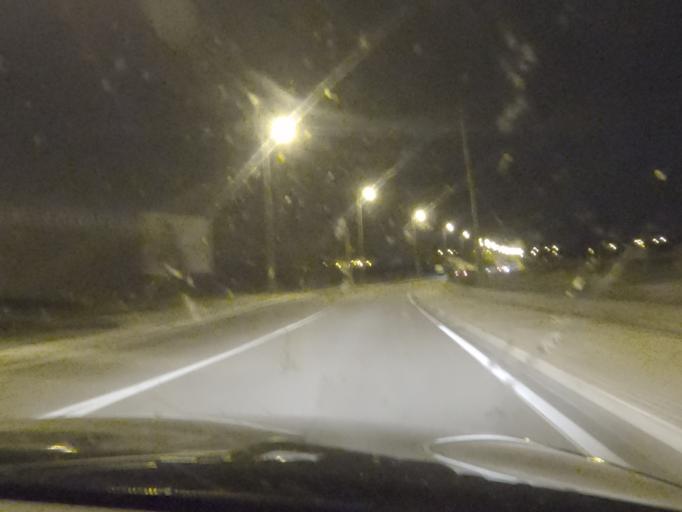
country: PT
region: Evora
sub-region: Estremoz
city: Estremoz
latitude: 38.8455
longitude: -7.6021
